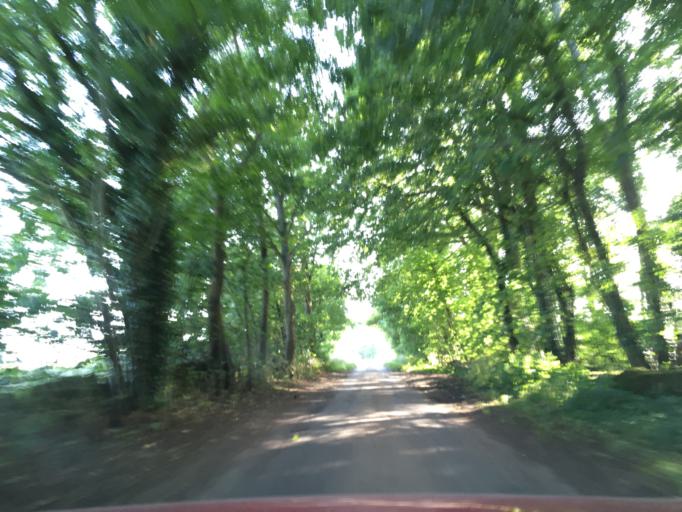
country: GB
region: England
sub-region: Gloucestershire
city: Lechlade
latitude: 51.7641
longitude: -1.7203
